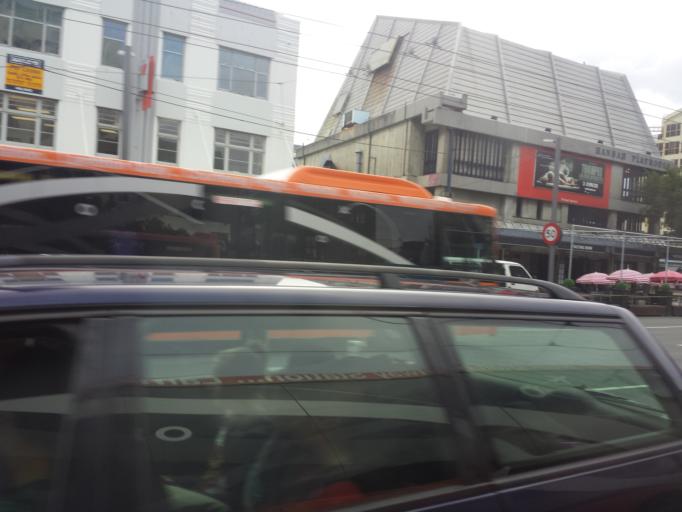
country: NZ
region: Wellington
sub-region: Wellington City
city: Wellington
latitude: -41.2940
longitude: 174.7831
